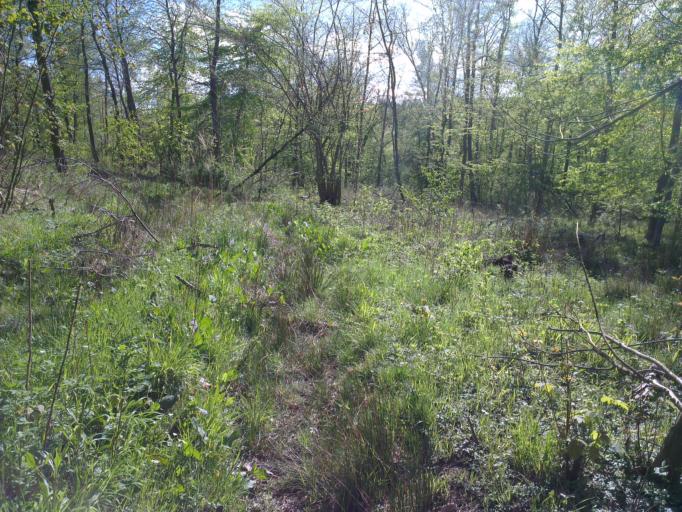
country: DK
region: Capital Region
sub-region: Frederikssund Kommune
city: Frederikssund
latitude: 55.8470
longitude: 12.0304
